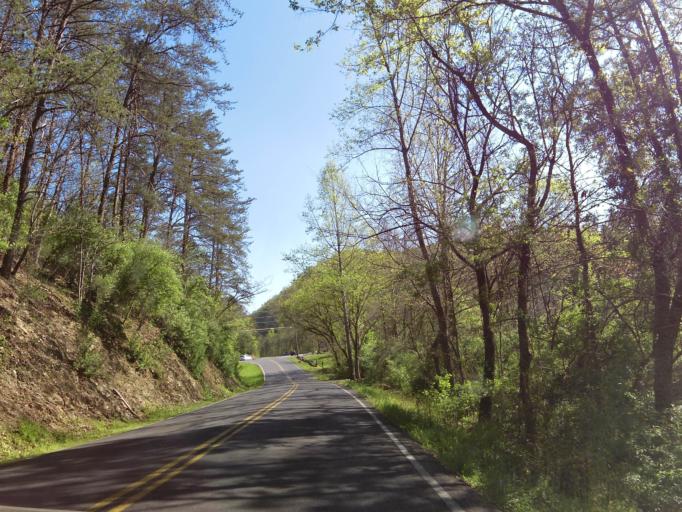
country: US
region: Tennessee
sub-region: Sevier County
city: Pigeon Forge
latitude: 35.7791
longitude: -83.6220
